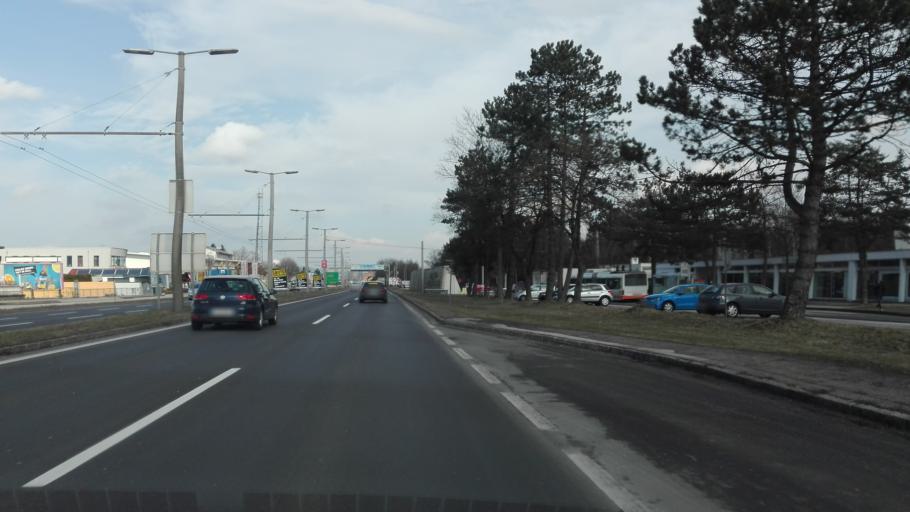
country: AT
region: Upper Austria
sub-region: Politischer Bezirk Linz-Land
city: Traun
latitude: 48.2391
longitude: 14.2462
